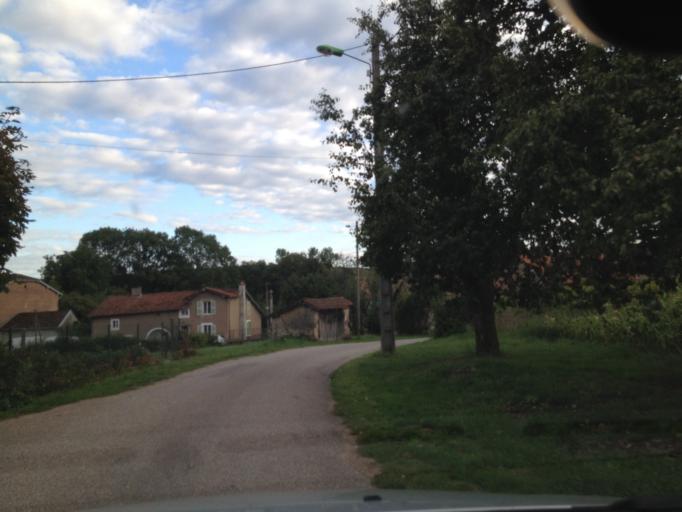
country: FR
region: Lorraine
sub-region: Departement des Vosges
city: Bains-les-Bains
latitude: 47.9740
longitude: 6.1771
